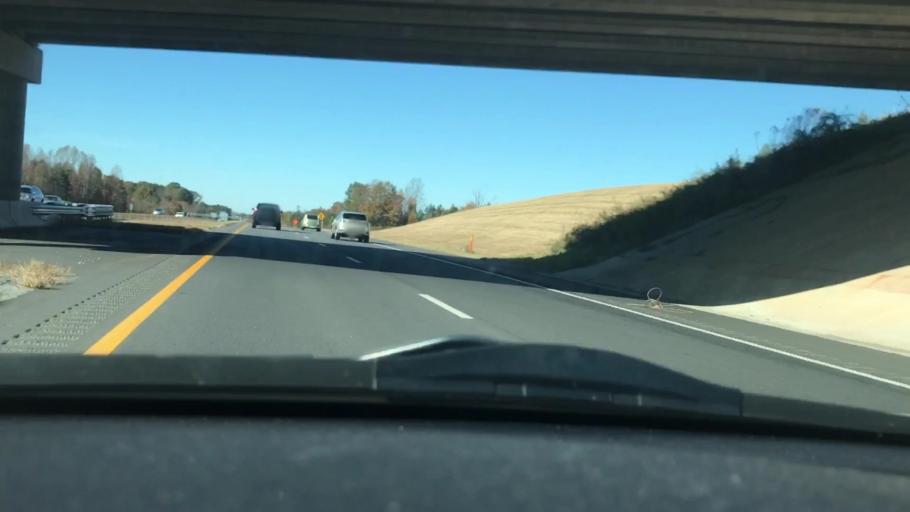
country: US
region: North Carolina
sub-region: Guilford County
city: Stokesdale
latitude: 36.2666
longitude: -79.9295
